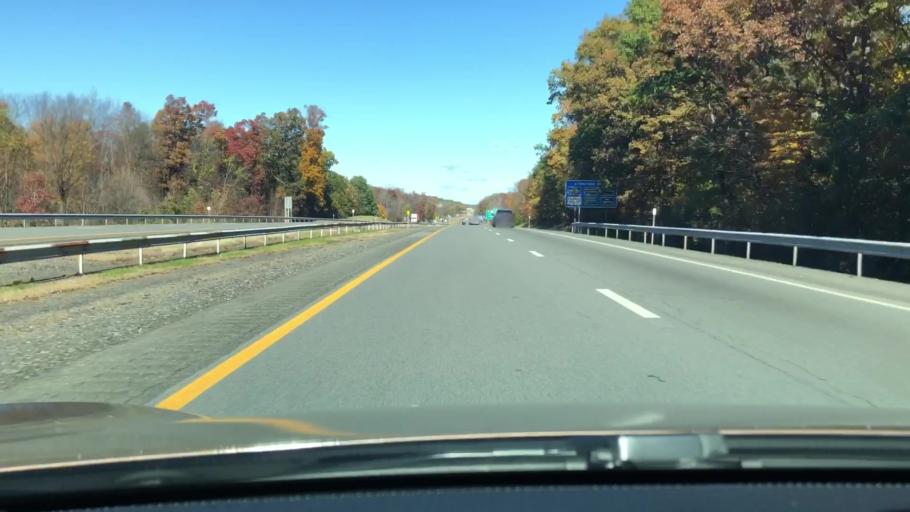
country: US
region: New York
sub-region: Orange County
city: Vails Gate
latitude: 41.4910
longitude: -74.0787
